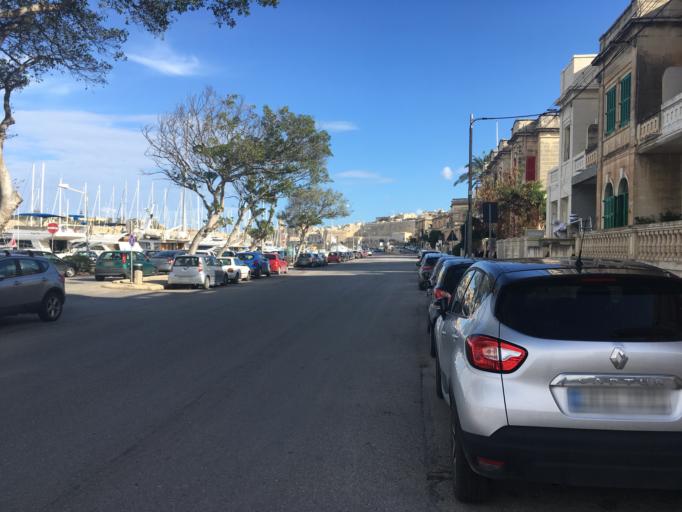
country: MT
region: Ta' Xbiex
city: Ta' Xbiex
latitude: 35.9009
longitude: 14.4967
